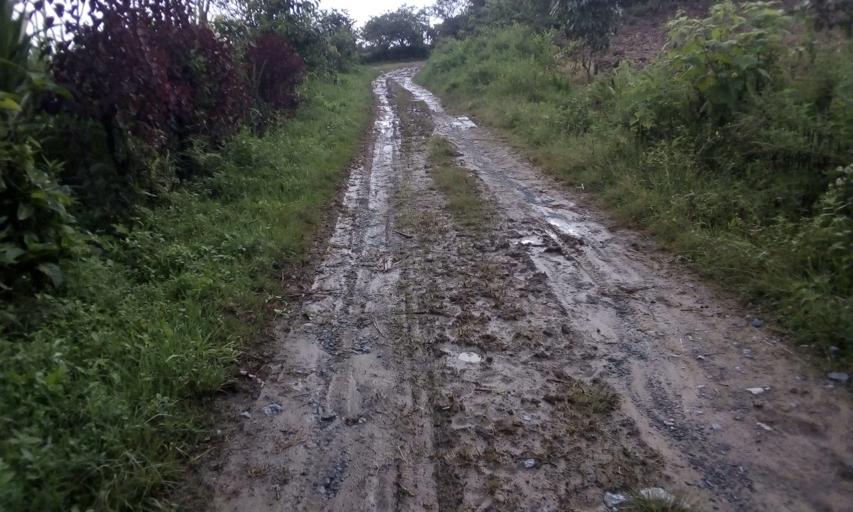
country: CO
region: Boyaca
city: Santana
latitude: 6.0045
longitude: -73.4955
